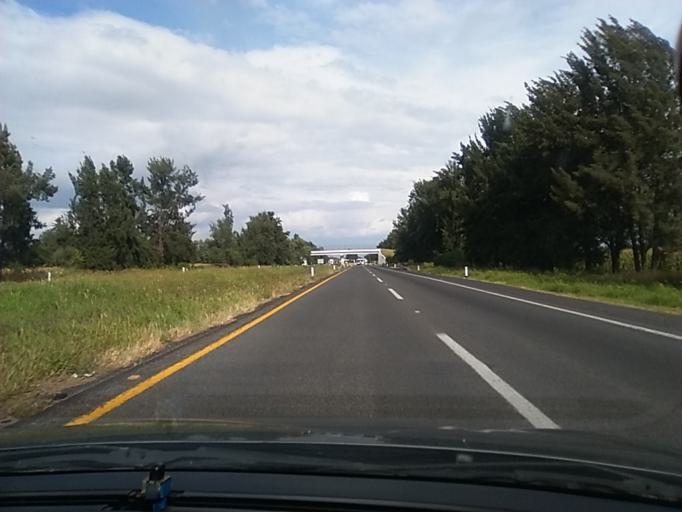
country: MX
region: Jalisco
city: La Barca
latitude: 20.3220
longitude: -102.5188
